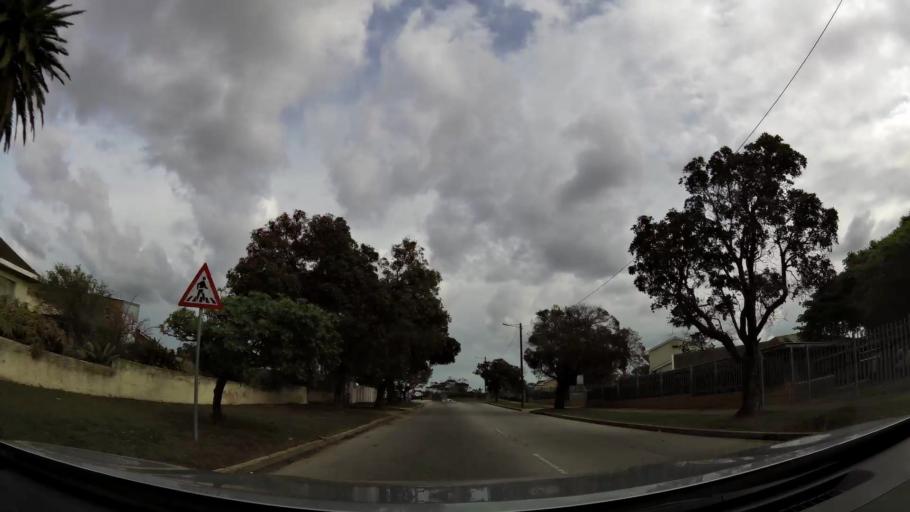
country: ZA
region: Eastern Cape
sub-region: Nelson Mandela Bay Metropolitan Municipality
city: Port Elizabeth
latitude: -33.9427
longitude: 25.5536
